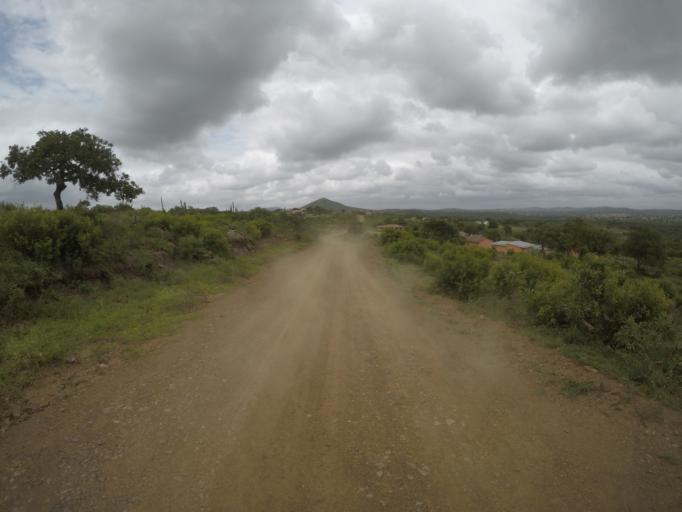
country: ZA
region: KwaZulu-Natal
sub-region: uThungulu District Municipality
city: Empangeni
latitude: -28.5803
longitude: 31.8669
